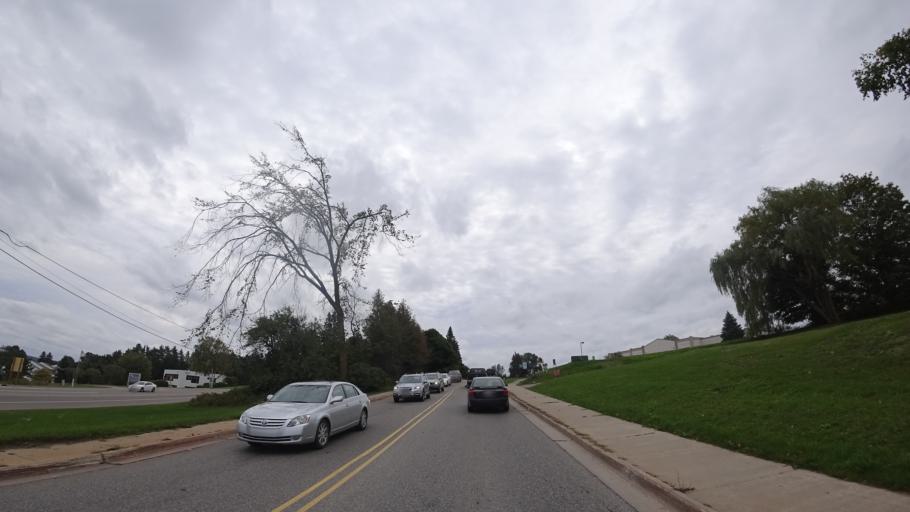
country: US
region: Michigan
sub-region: Emmet County
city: Petoskey
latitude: 45.3598
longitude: -84.9709
